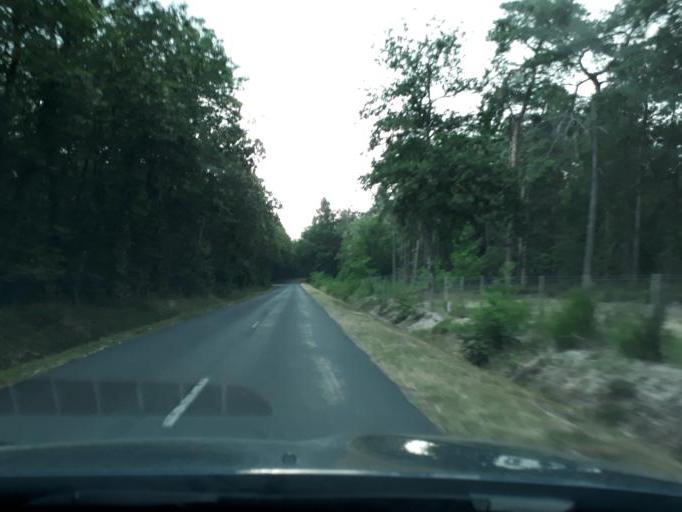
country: FR
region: Centre
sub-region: Departement du Loiret
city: Marcilly-en-Villette
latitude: 47.7531
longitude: 2.0568
